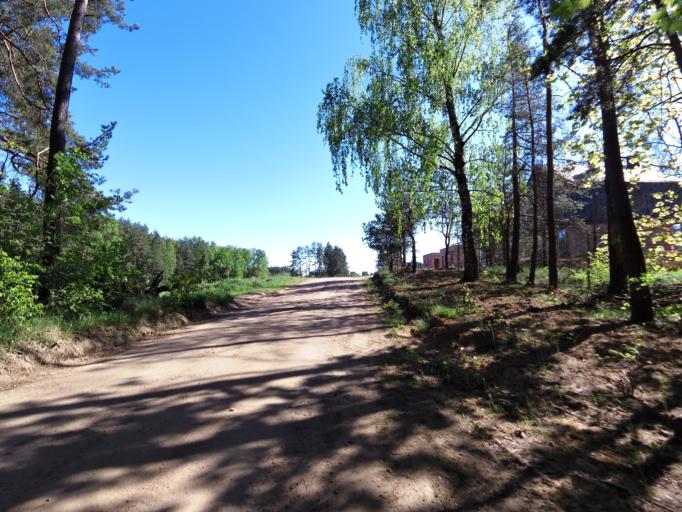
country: LT
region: Vilnius County
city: Pilaite
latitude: 54.6876
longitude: 25.1629
